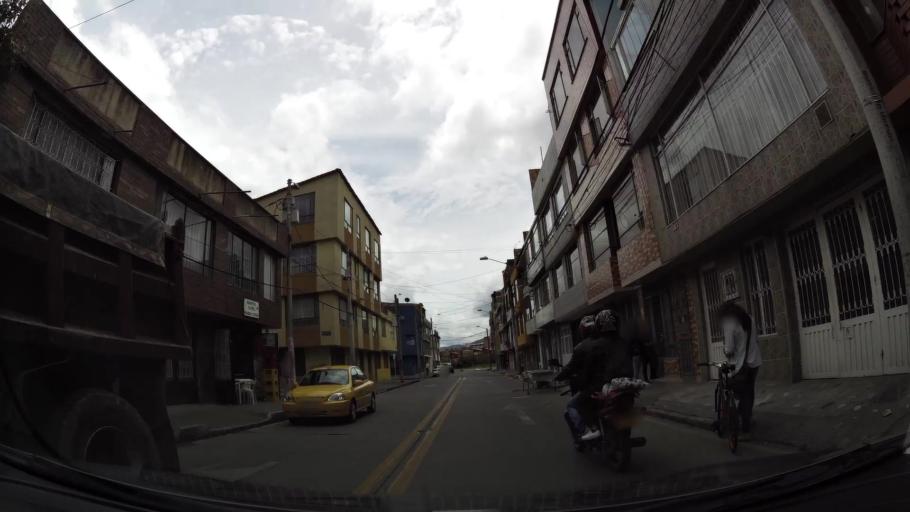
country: CO
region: Cundinamarca
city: Funza
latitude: 4.7039
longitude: -74.1222
